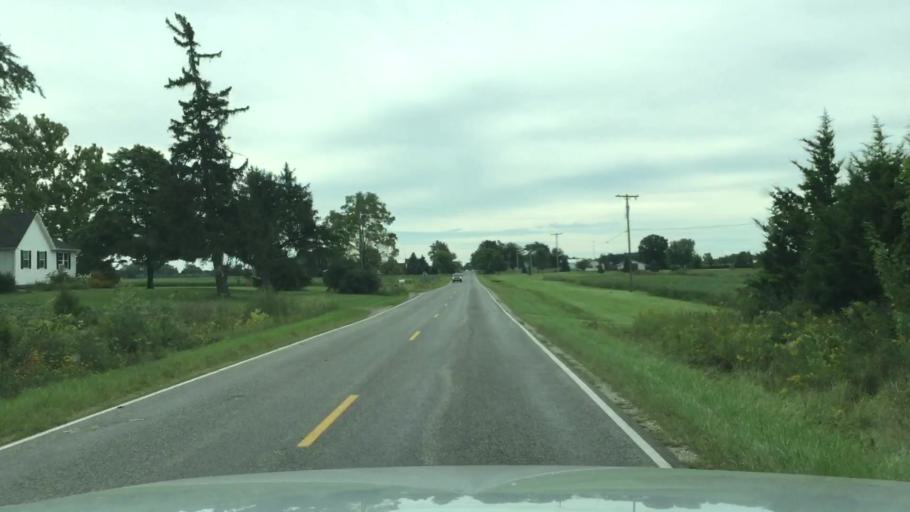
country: US
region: Michigan
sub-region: Genesee County
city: Flushing
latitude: 43.0553
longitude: -83.9875
